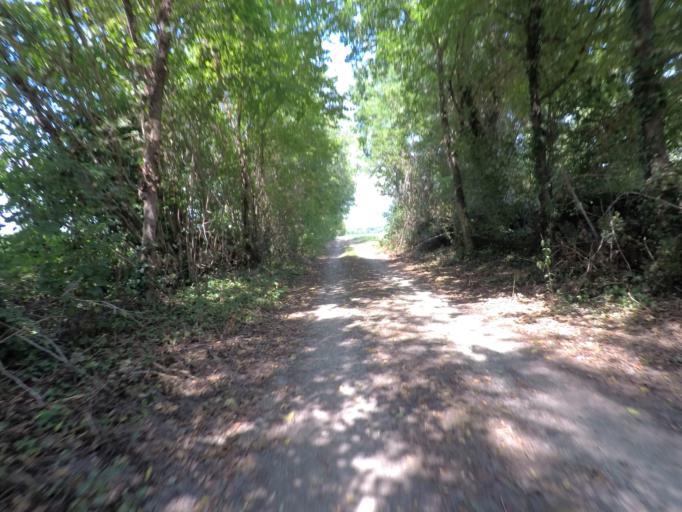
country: IT
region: Friuli Venezia Giulia
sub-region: Provincia di Pordenone
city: Lestans
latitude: 46.1444
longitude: 12.9082
